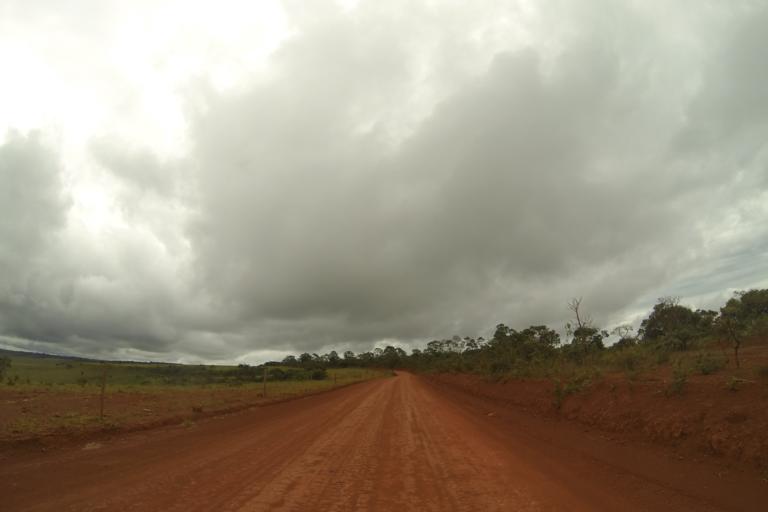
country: BR
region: Minas Gerais
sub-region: Campos Altos
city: Campos Altos
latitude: -19.8440
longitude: -46.3228
